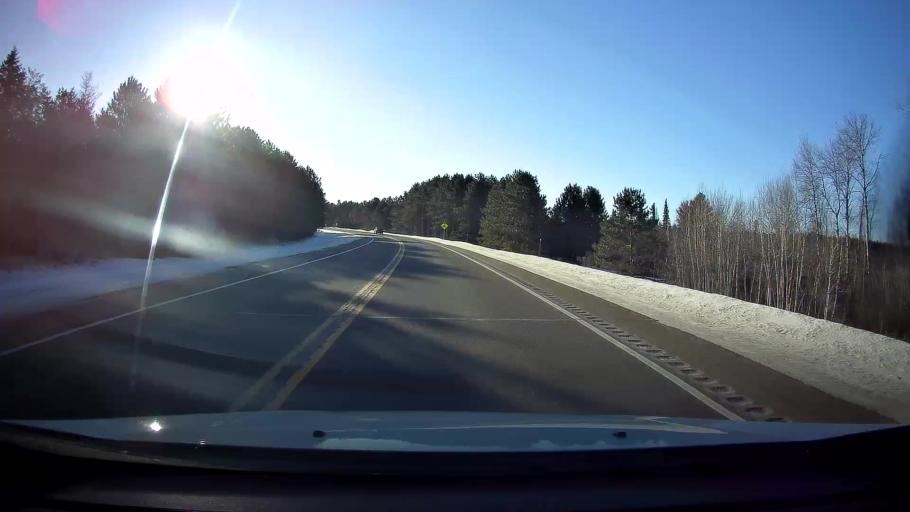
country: US
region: Wisconsin
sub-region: Sawyer County
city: Hayward
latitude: 45.9909
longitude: -91.5931
